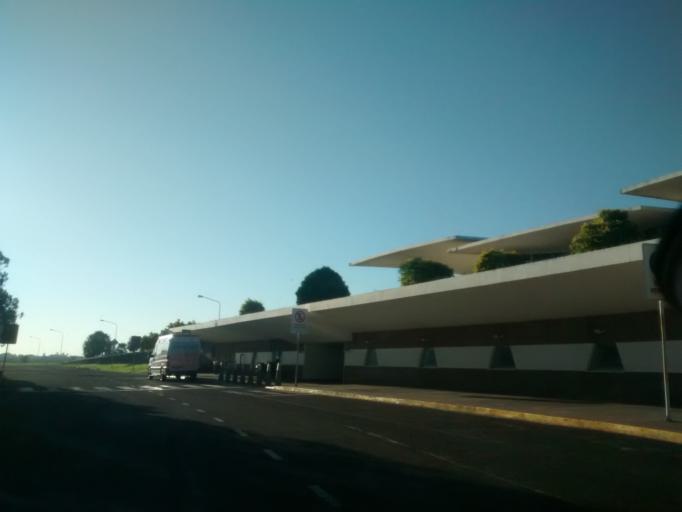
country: AR
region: Chaco
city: Fontana
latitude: -27.4445
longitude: -59.0485
